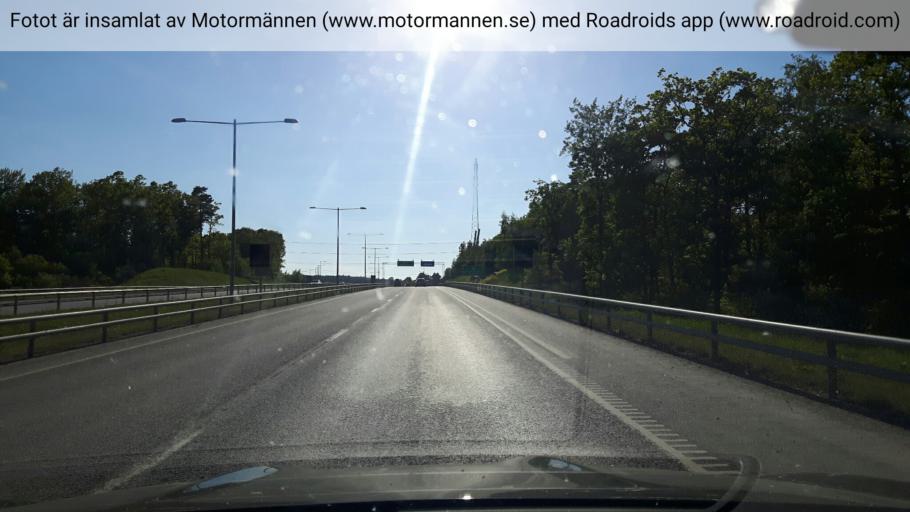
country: SE
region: Stockholm
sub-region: Taby Kommun
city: Taby
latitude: 59.4747
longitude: 18.0097
